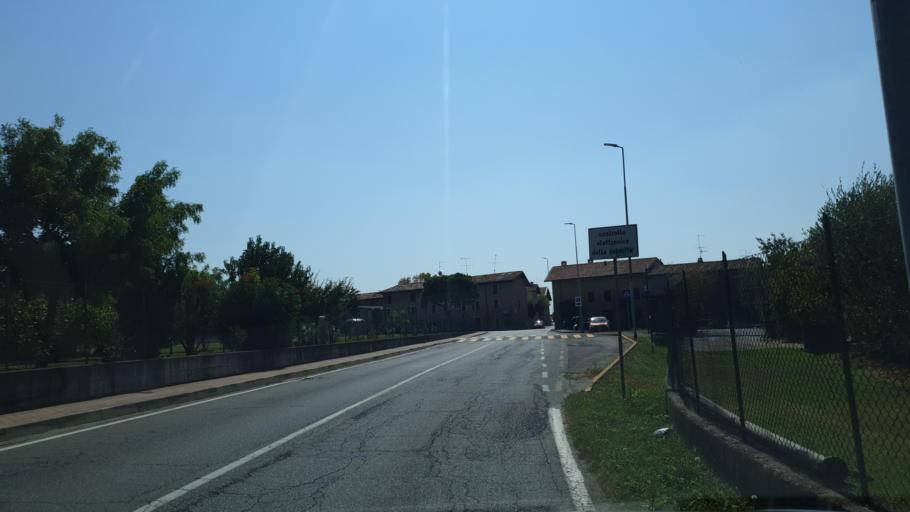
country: IT
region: Lombardy
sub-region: Provincia di Brescia
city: Carzago Riviera
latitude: 45.5239
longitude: 10.4598
